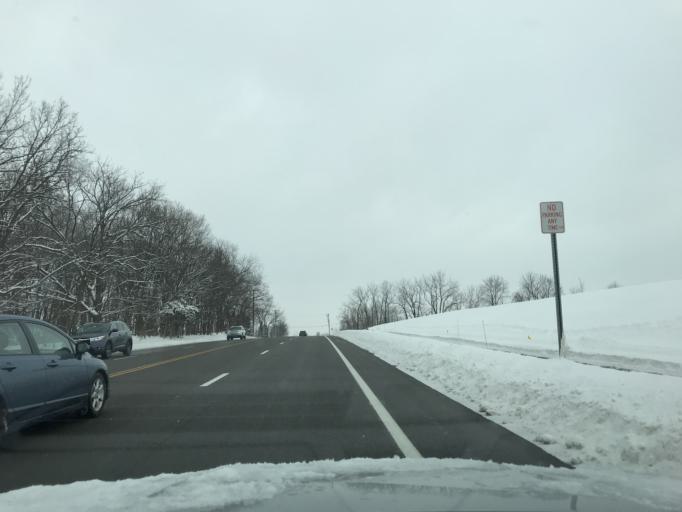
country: US
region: Wisconsin
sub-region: Dane County
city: Sun Prairie
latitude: 43.1601
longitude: -89.2851
